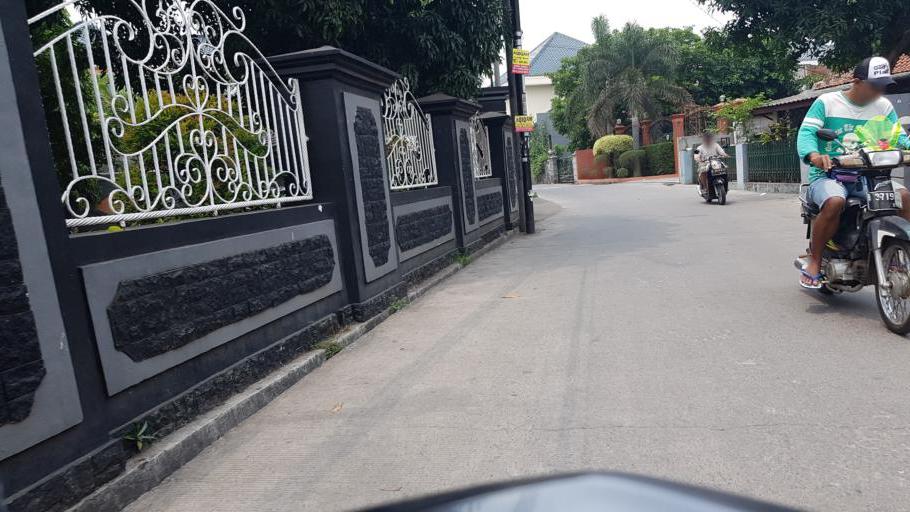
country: ID
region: West Java
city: Bekasi
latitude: -6.2790
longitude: 106.9303
